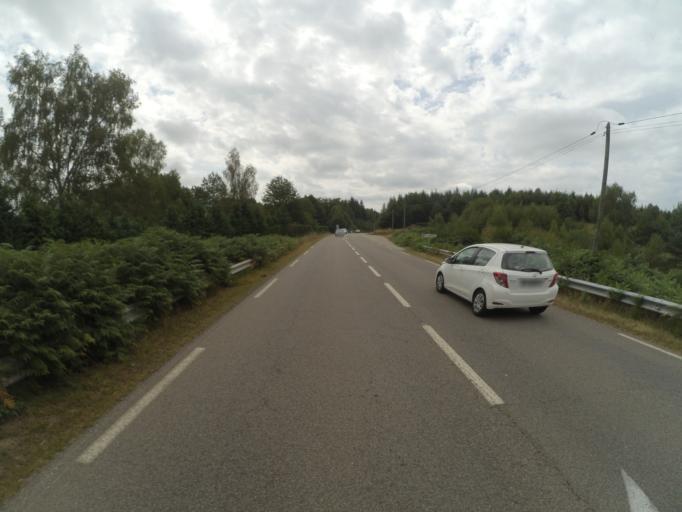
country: FR
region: Limousin
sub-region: Departement de la Correze
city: Ussel
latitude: 45.6133
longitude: 2.2933
